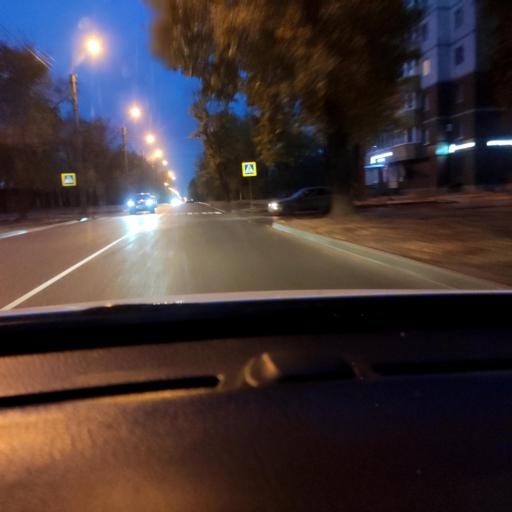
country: RU
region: Voronezj
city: Voronezh
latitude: 51.6546
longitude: 39.2473
